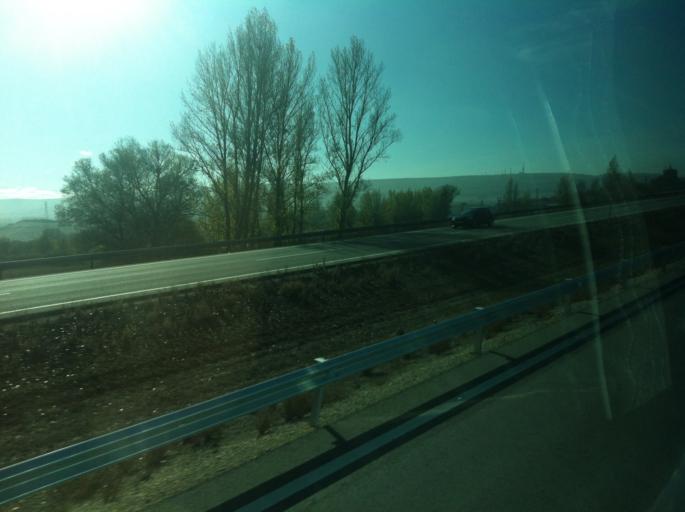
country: ES
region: Castille and Leon
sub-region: Provincia de Burgos
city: Quintanapalla
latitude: 42.4139
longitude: -3.5285
